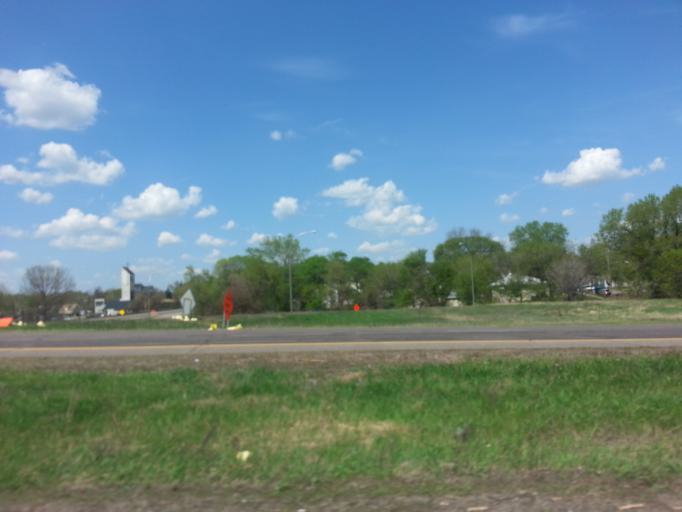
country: US
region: Minnesota
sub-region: Hennepin County
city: Richfield
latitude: 44.8959
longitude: -93.2455
